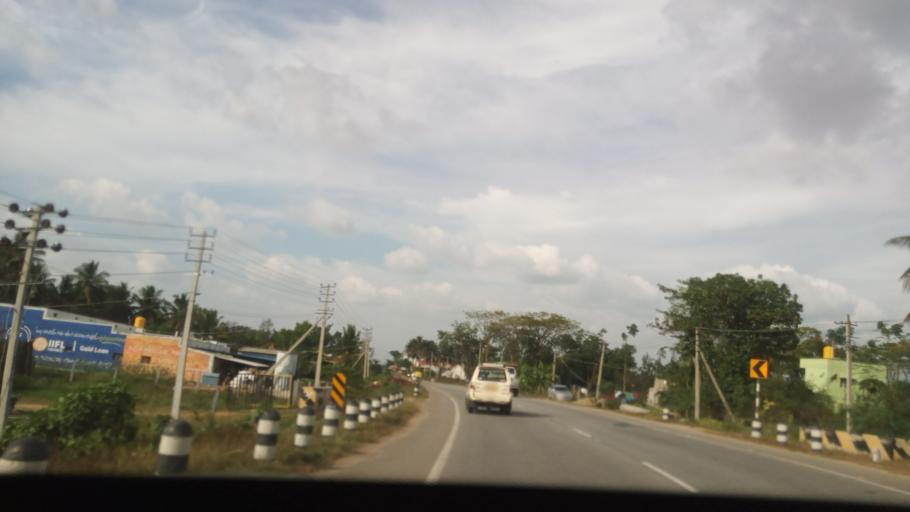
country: IN
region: Karnataka
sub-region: Mandya
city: Maddur
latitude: 12.6787
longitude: 77.0590
